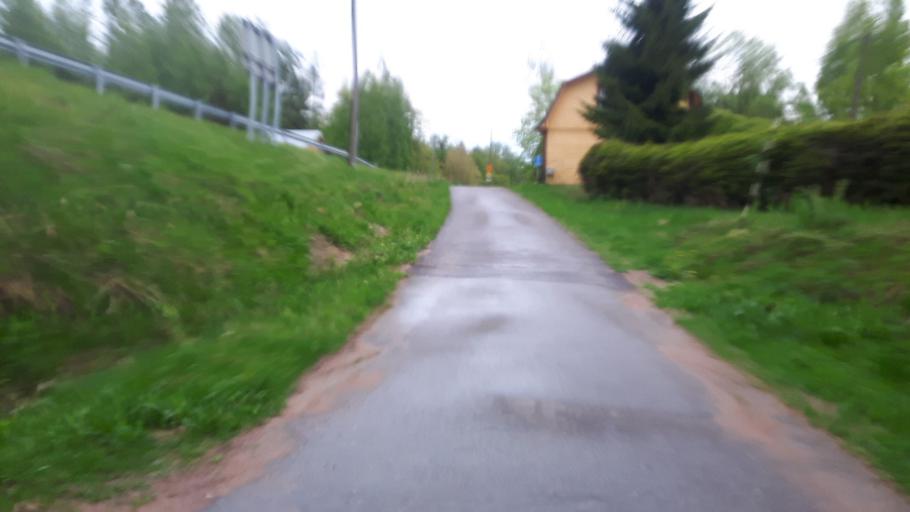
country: FI
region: Kymenlaakso
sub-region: Kotka-Hamina
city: Hamina
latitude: 60.5655
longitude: 27.0953
